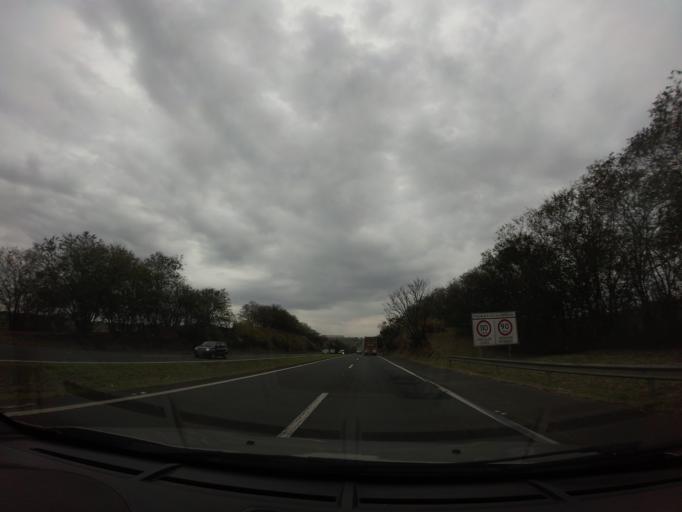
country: BR
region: Sao Paulo
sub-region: Santa Barbara D'Oeste
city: Santa Barbara d'Oeste
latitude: -22.7538
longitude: -47.4851
